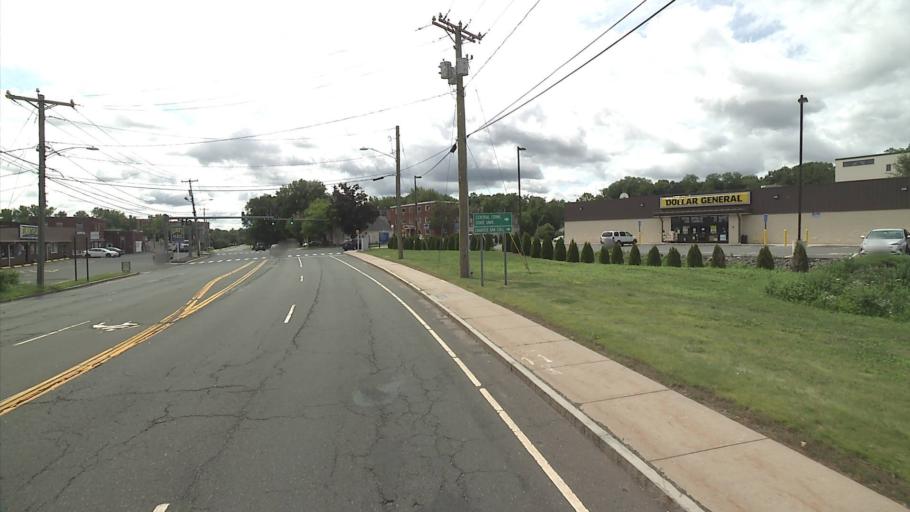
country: US
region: Connecticut
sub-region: Hartford County
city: Newington
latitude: 41.6921
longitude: -72.7598
